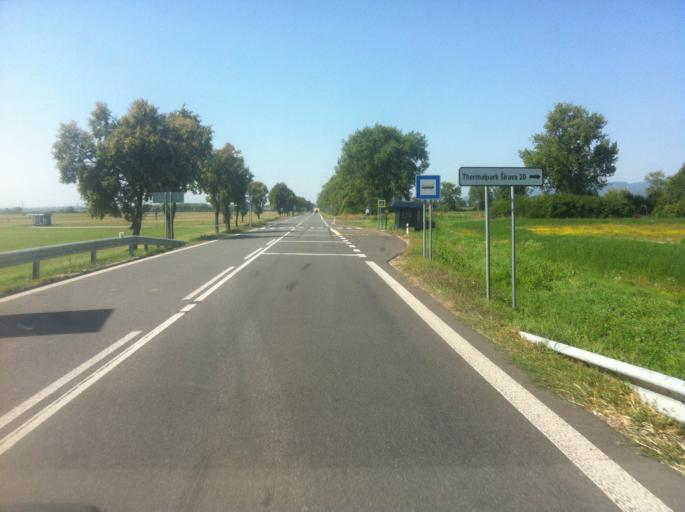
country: SK
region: Kosicky
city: Sobrance
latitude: 48.7604
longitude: 22.1238
